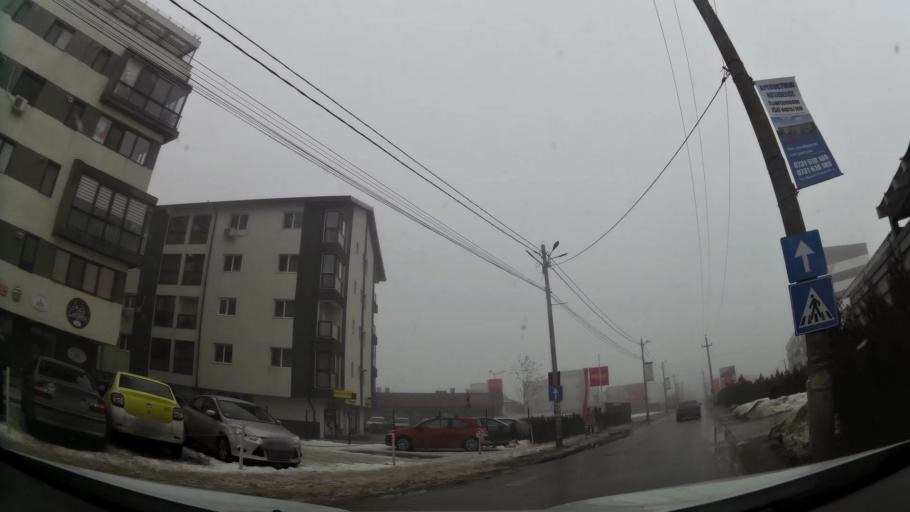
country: RO
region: Ilfov
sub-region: Comuna Chiajna
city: Chiajna
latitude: 44.4491
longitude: 25.9867
